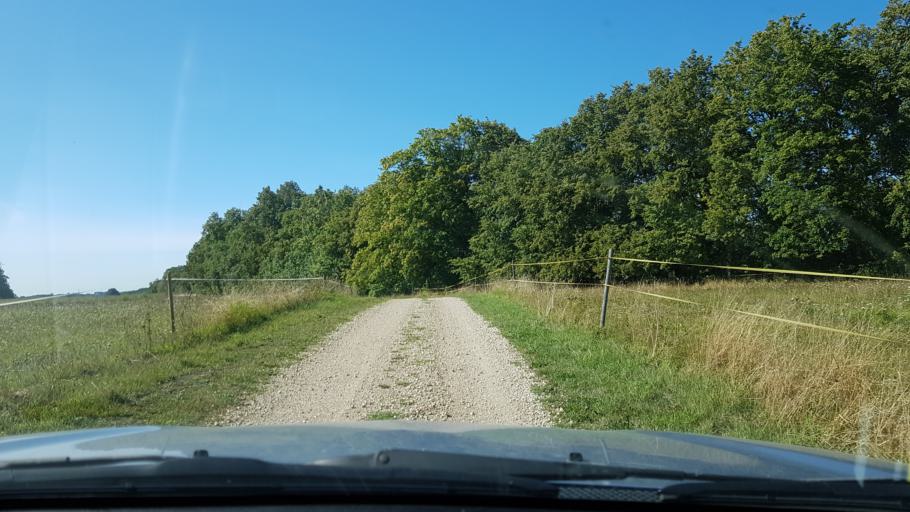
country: EE
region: Ida-Virumaa
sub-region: Sillamaee linn
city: Sillamae
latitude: 59.3948
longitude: 27.8523
